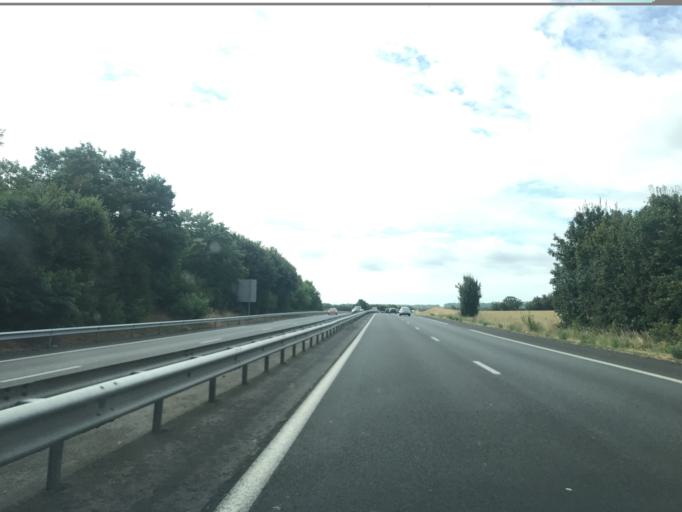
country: FR
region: Poitou-Charentes
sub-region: Departement des Deux-Sevres
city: Sauze-Vaussais
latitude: 46.1277
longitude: 0.1812
